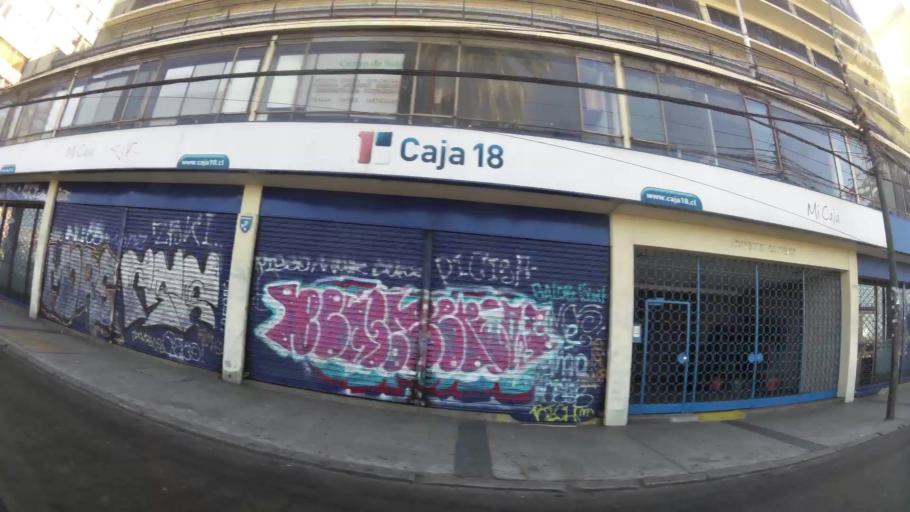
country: CL
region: Valparaiso
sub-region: Provincia de Valparaiso
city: Valparaiso
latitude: -33.0421
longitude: -71.6232
